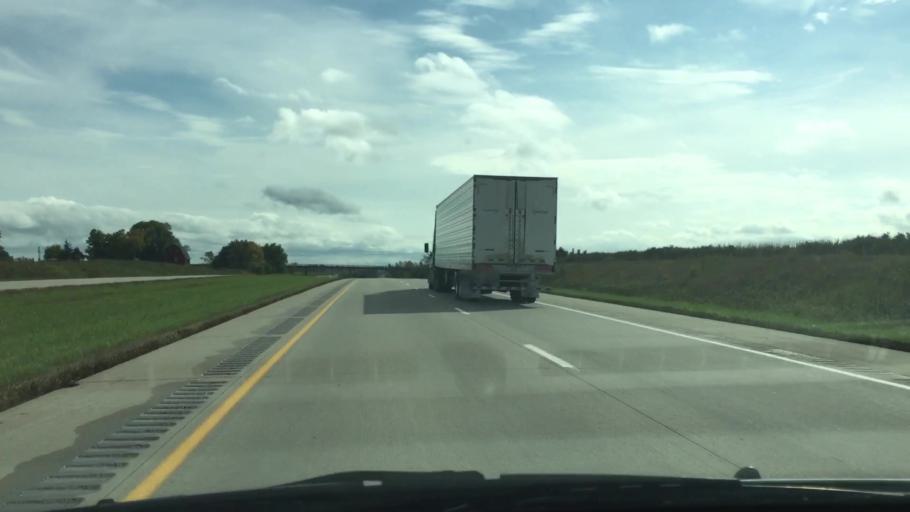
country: US
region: Iowa
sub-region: Clarke County
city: Osceola
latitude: 40.9176
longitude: -93.7974
